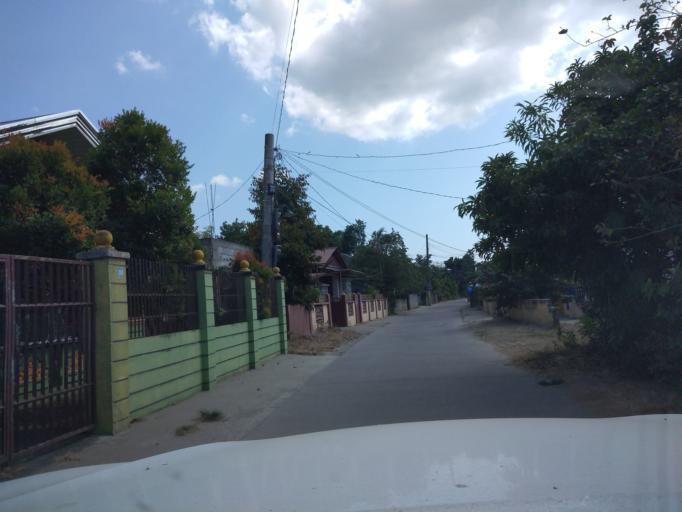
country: PH
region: Central Luzon
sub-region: Province of Pampanga
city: Candaba
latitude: 15.0903
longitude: 120.8150
